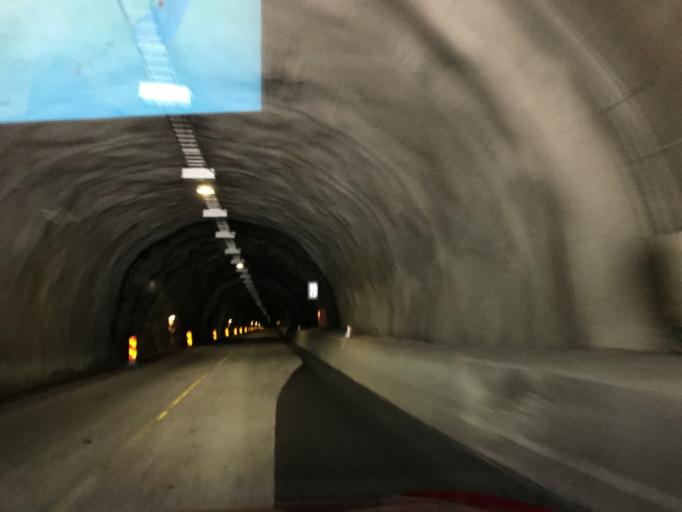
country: NO
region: Hordaland
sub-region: Eidfjord
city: Eidfjord
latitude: 60.4424
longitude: 7.1067
